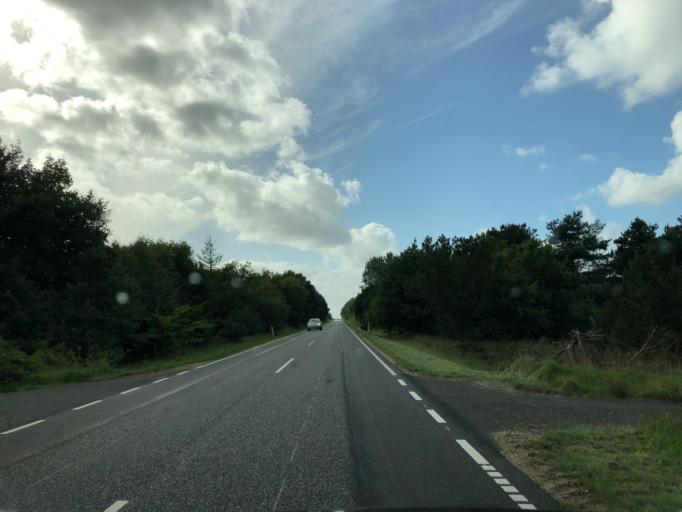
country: DK
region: Central Jutland
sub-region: Holstebro Kommune
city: Holstebro
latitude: 56.3707
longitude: 8.4916
